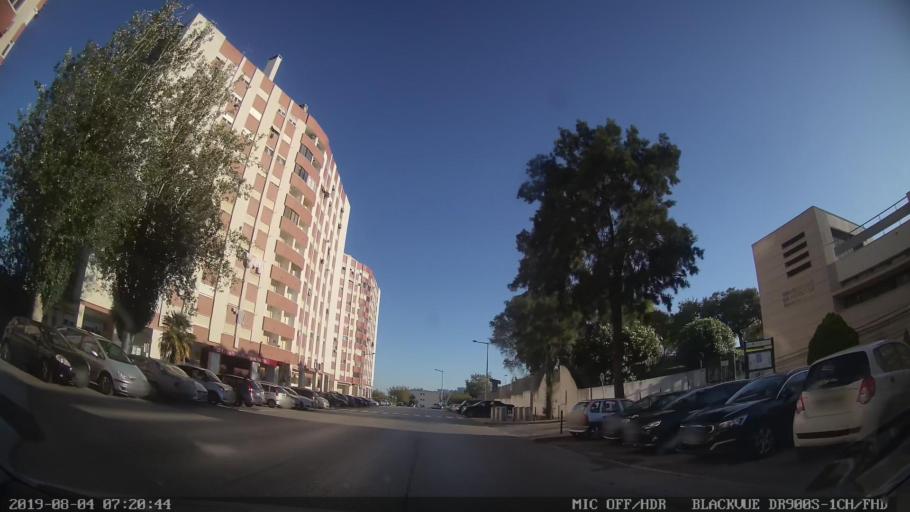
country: PT
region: Lisbon
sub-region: Vila Franca de Xira
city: Povoa de Santa Iria
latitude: 38.8619
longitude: -9.0680
